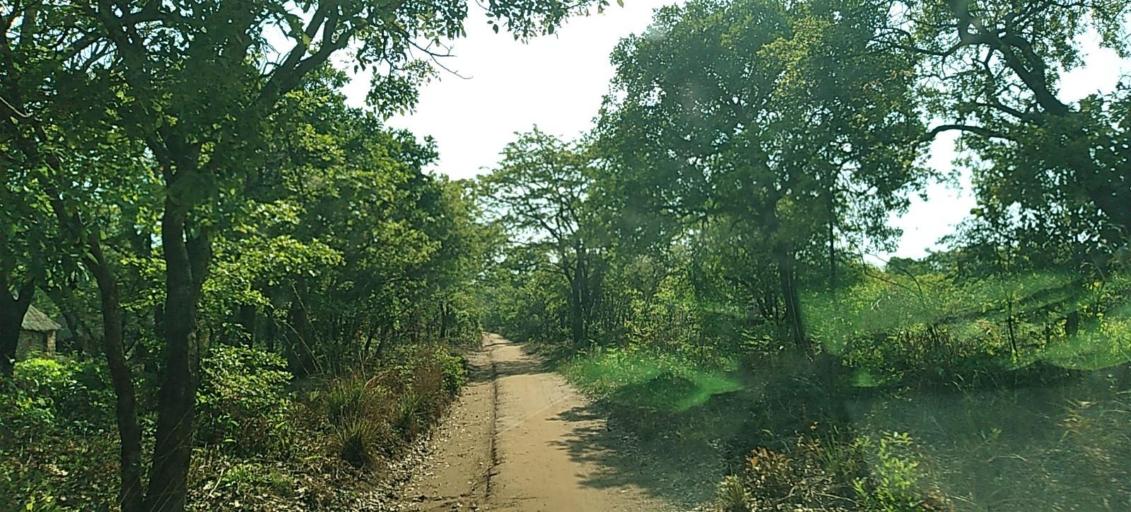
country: ZM
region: North-Western
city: Mwinilunga
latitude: -11.3001
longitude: 24.8506
